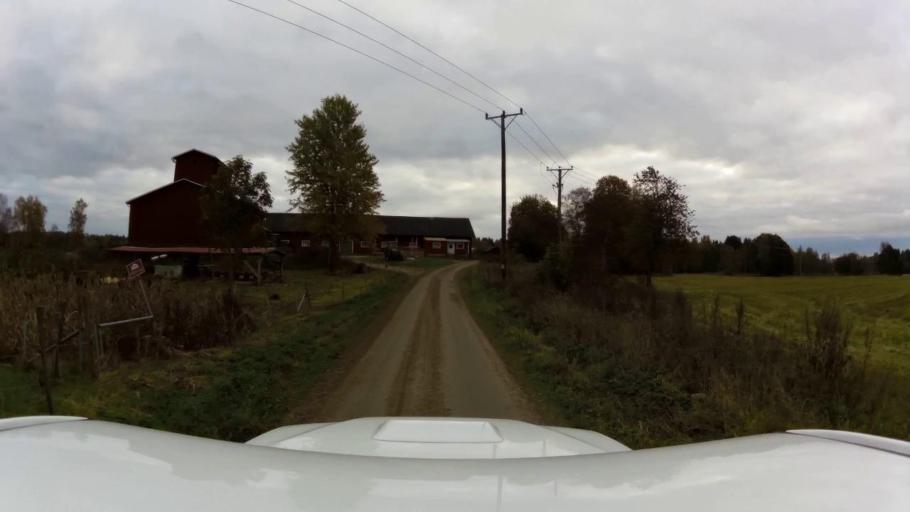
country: SE
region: OEstergoetland
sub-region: Linkopings Kommun
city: Ljungsbro
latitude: 58.5562
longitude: 15.4196
